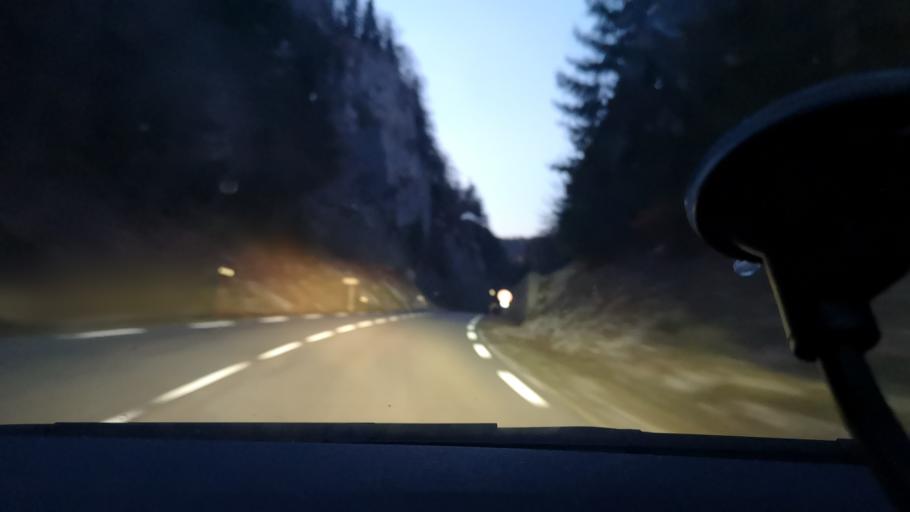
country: FR
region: Franche-Comte
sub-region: Departement du Jura
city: Champagnole
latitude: 46.7529
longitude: 5.9696
